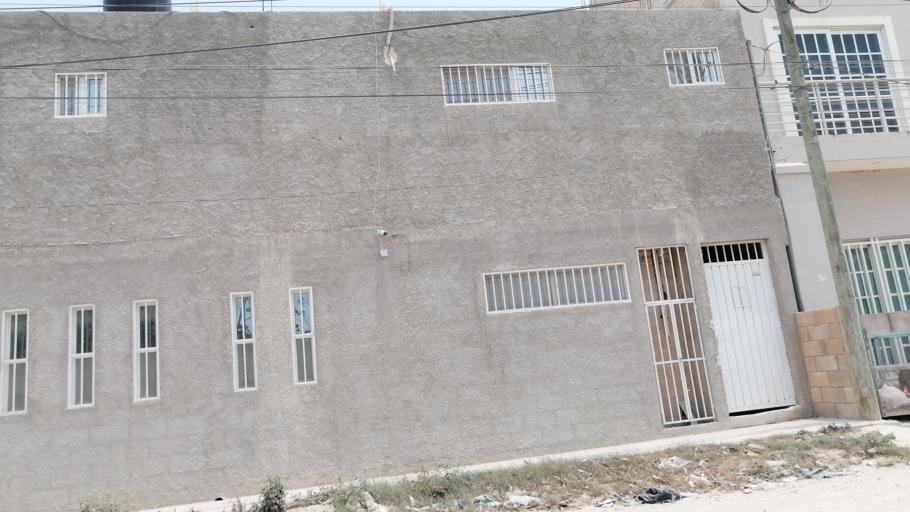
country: MX
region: Quintana Roo
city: Cancun
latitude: 21.1372
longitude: -86.8980
